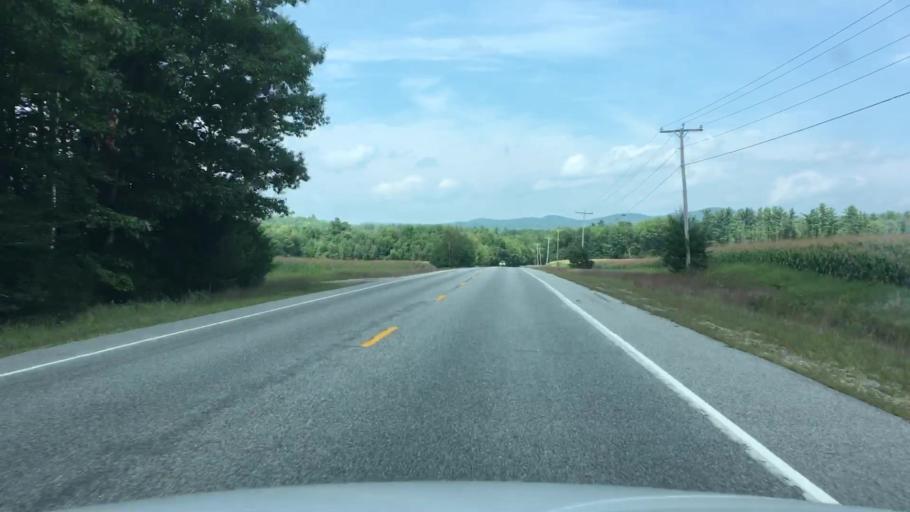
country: US
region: Maine
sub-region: Oxford County
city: Canton
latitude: 44.4693
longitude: -70.3239
